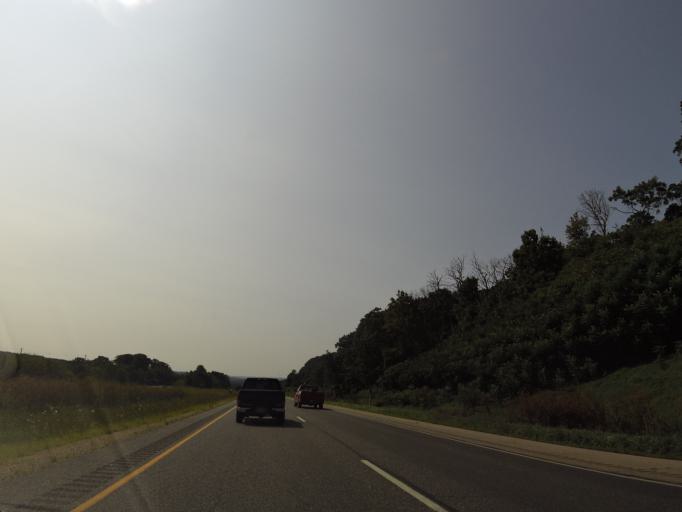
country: US
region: Wisconsin
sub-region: Monroe County
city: Tomah
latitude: 43.9392
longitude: -90.6089
